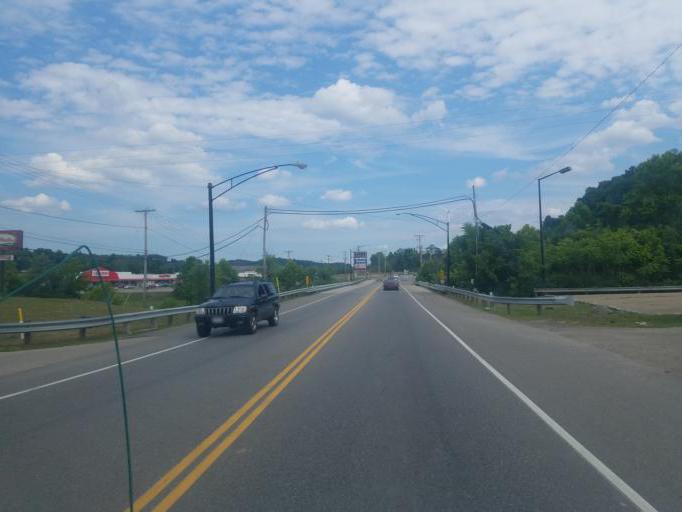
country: US
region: Ohio
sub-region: Guernsey County
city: Cambridge
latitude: 40.0088
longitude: -81.5797
